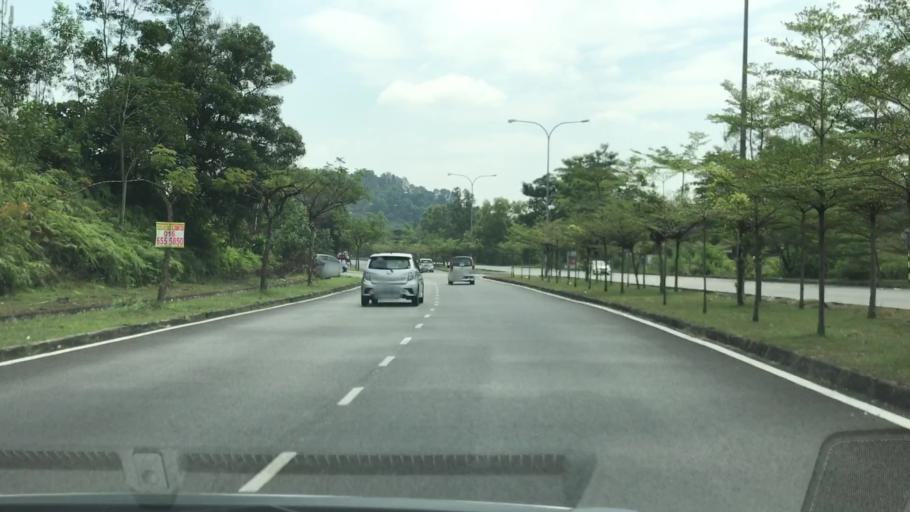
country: MY
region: Putrajaya
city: Putrajaya
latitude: 3.0075
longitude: 101.6703
